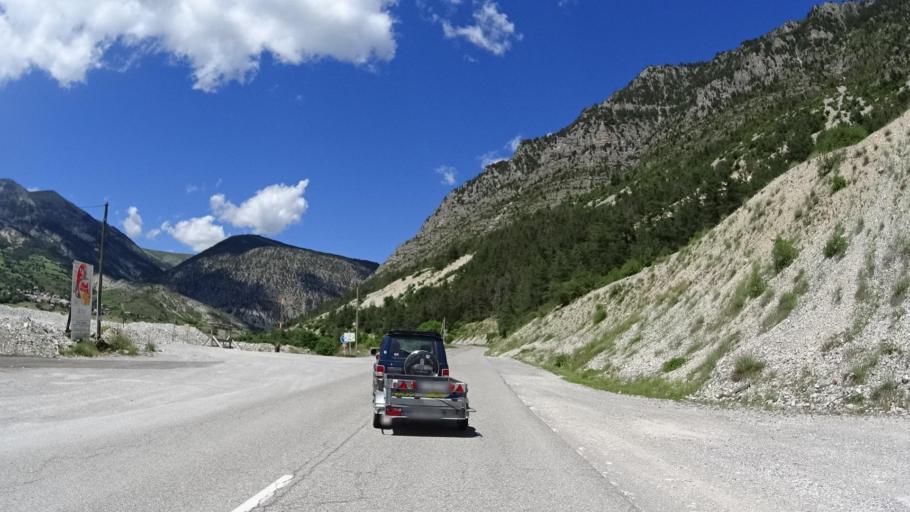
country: FR
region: Provence-Alpes-Cote d'Azur
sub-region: Departement des Alpes-de-Haute-Provence
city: Annot
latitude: 44.0839
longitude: 6.5673
